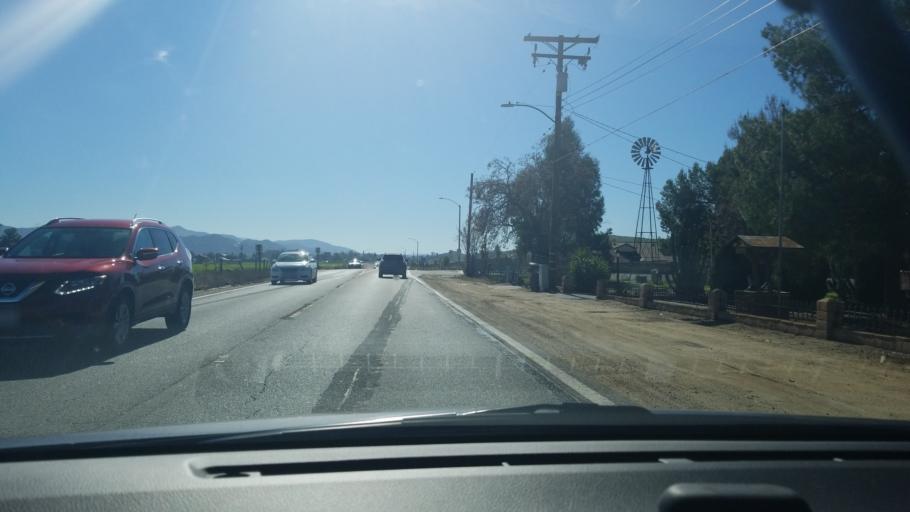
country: US
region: California
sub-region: Riverside County
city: Green Acres
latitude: 33.7334
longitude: -117.0764
